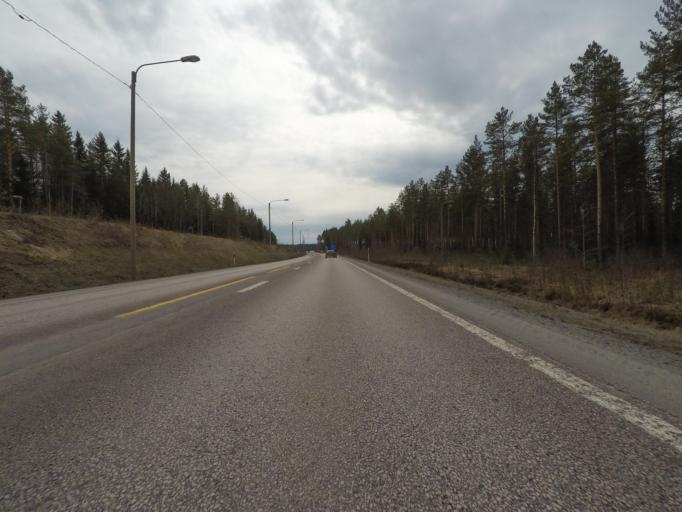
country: FI
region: Paijanne Tavastia
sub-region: Lahti
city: Hartola
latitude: 61.5717
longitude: 26.0048
